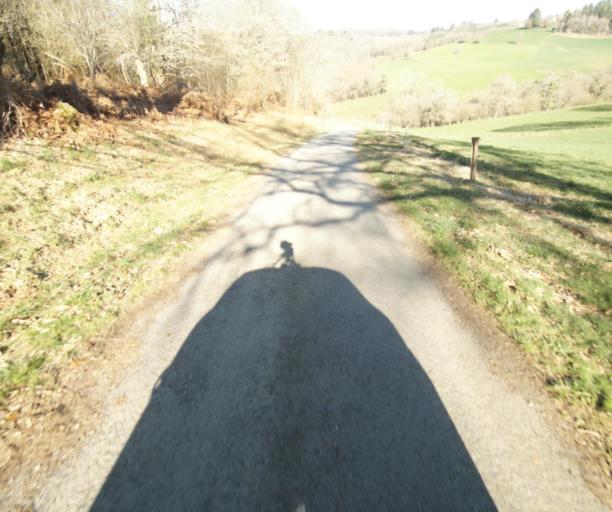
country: FR
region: Limousin
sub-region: Departement de la Correze
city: Seilhac
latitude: 45.3810
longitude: 1.7743
